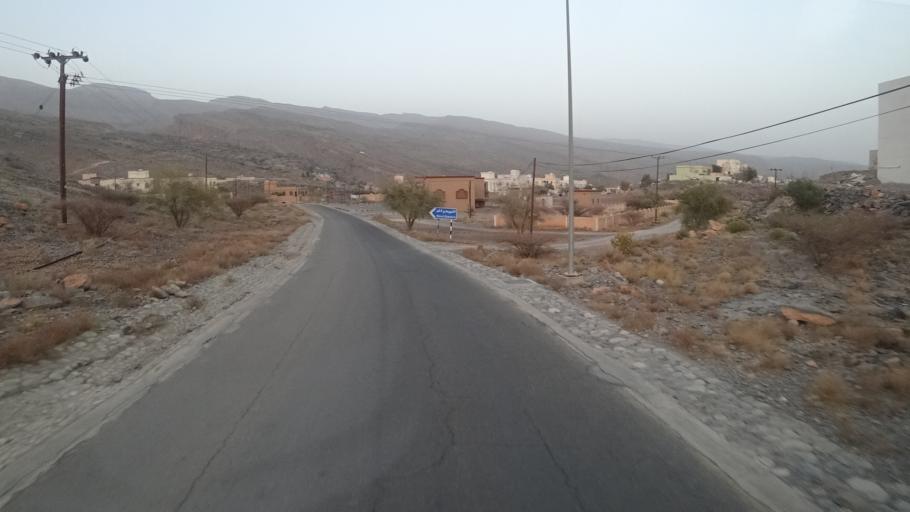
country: OM
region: Muhafazat ad Dakhiliyah
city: Bahla'
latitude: 23.1368
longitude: 57.3046
